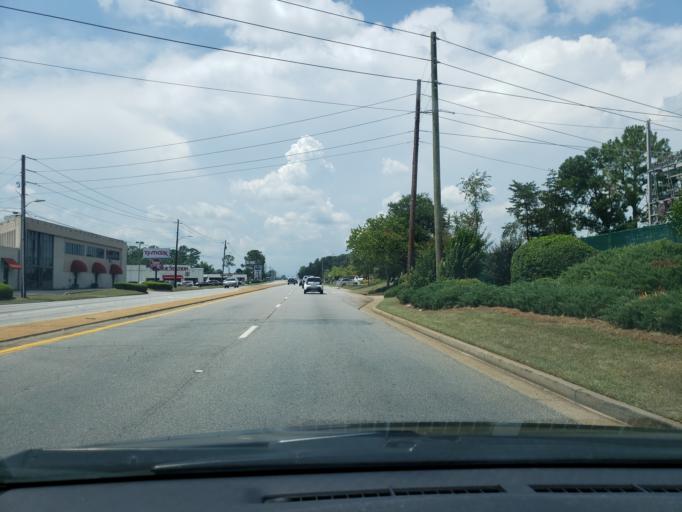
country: US
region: Georgia
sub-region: Dougherty County
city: Albany
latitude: 31.6137
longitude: -84.2160
